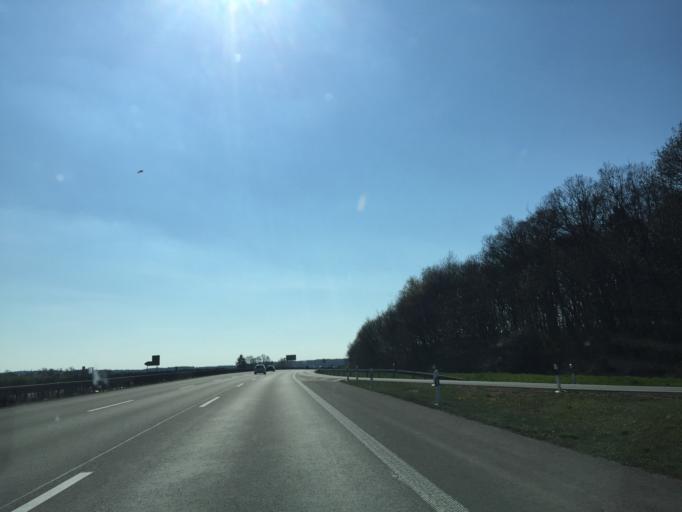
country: DE
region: Thuringia
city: Klettbach
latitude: 50.9256
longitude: 11.1365
